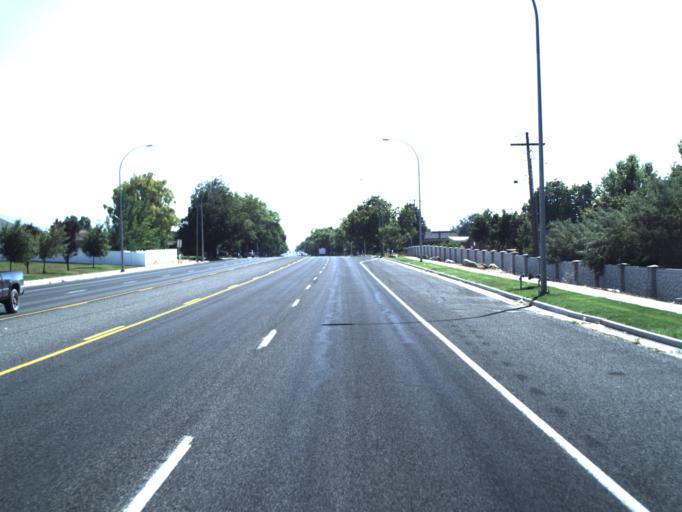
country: US
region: Utah
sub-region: Cache County
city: Smithfield
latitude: 41.8487
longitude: -111.8323
